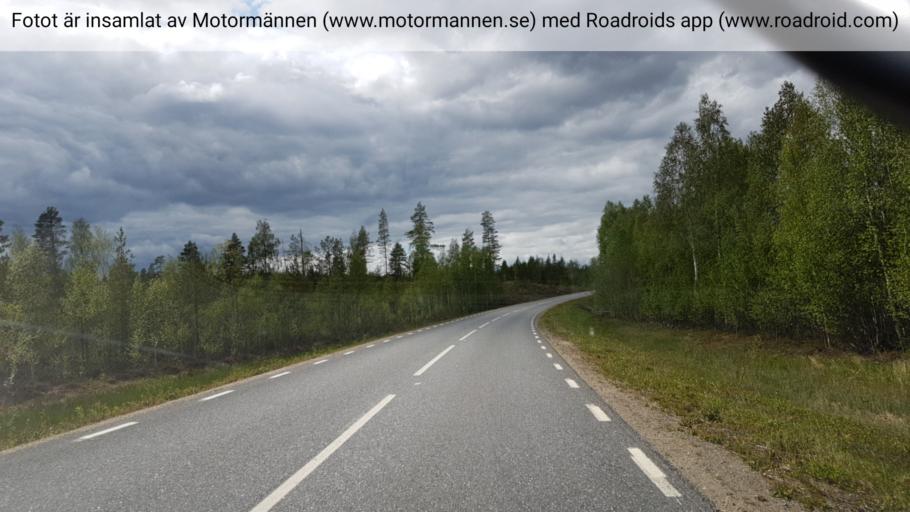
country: SE
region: Vaesterbotten
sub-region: Vindelns Kommun
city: Vindeln
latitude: 64.5228
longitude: 19.8260
